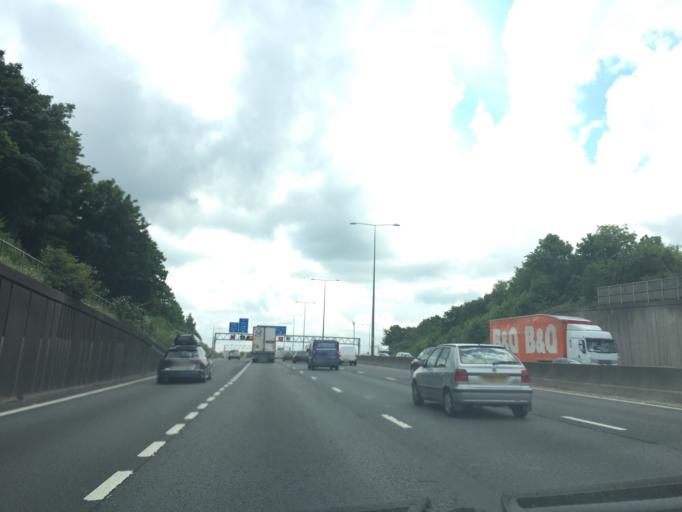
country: GB
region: England
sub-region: Greater London
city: High Barnet
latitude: 51.6911
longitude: -0.2357
